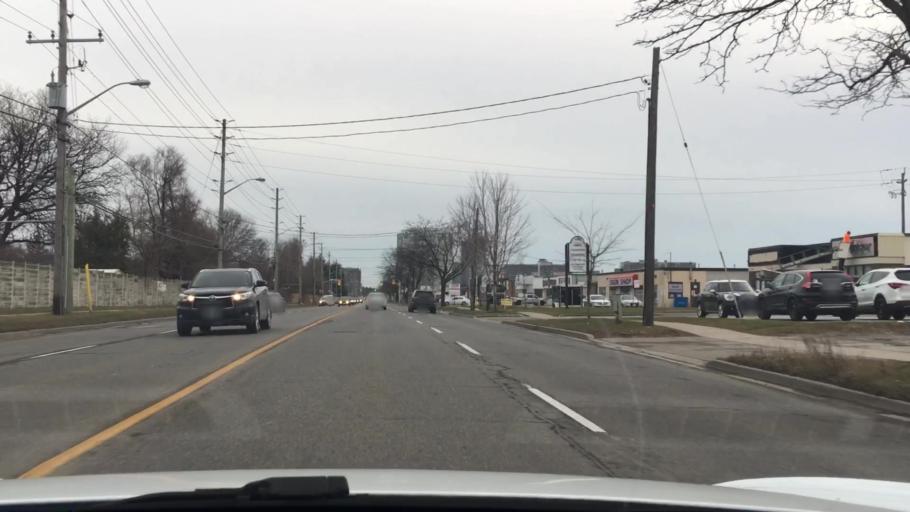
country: CA
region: Ontario
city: Scarborough
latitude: 43.7599
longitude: -79.2683
